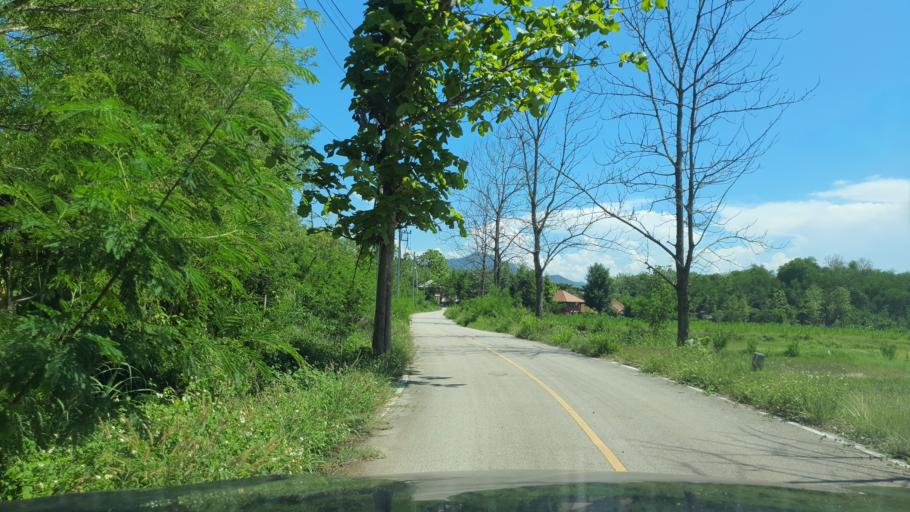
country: TH
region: Chiang Mai
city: Mae On
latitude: 18.7922
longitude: 99.2644
